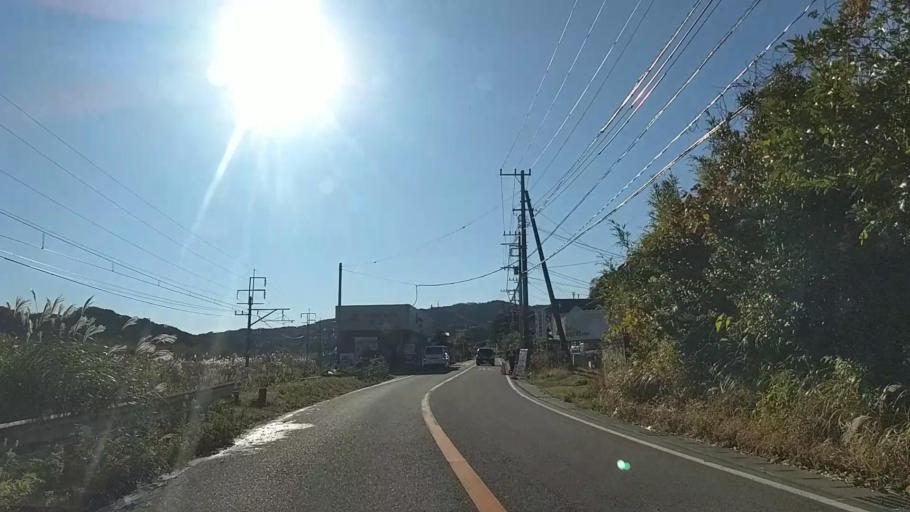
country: JP
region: Chiba
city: Futtsu
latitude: 35.2772
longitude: 139.8612
